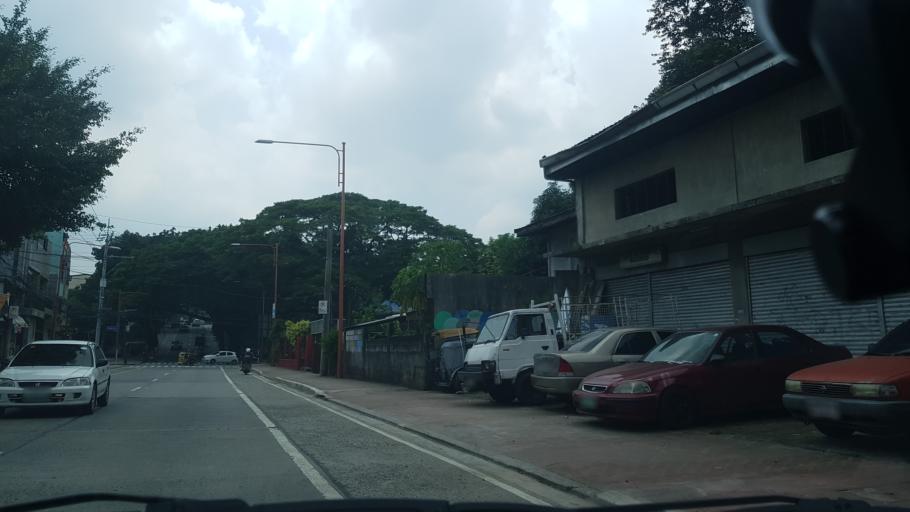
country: PH
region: Calabarzon
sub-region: Province of Rizal
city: Antipolo
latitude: 14.6488
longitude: 121.1211
